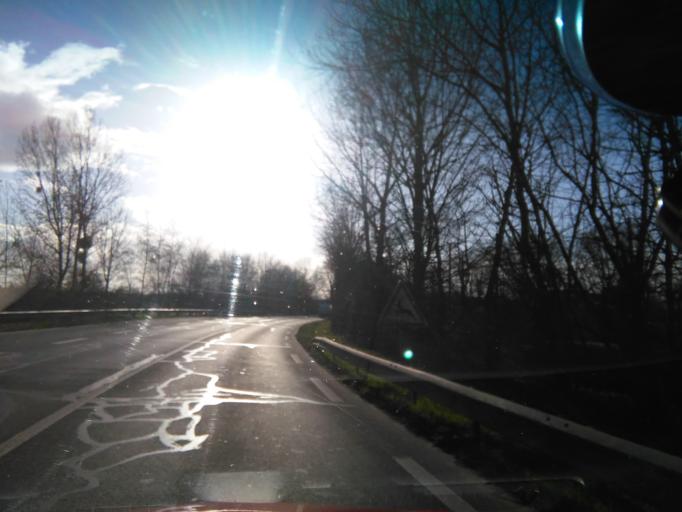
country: FR
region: Lower Normandy
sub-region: Departement du Calvados
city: Louvigny
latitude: 49.1662
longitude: -0.3868
